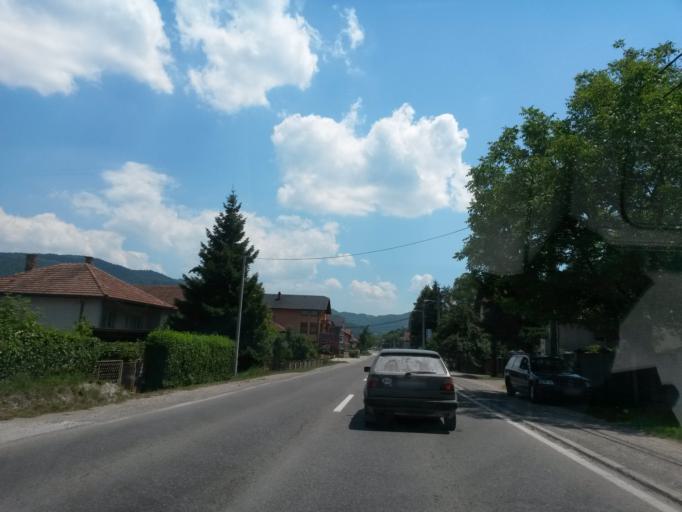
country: BA
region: Republika Srpska
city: Doboj
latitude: 44.7550
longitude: 18.0800
